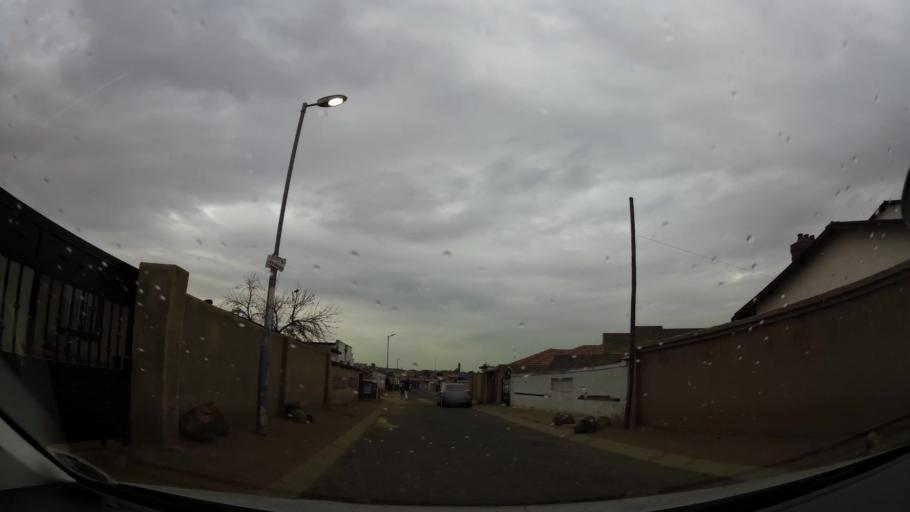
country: ZA
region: Gauteng
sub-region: City of Johannesburg Metropolitan Municipality
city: Soweto
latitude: -26.2542
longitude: 27.8648
